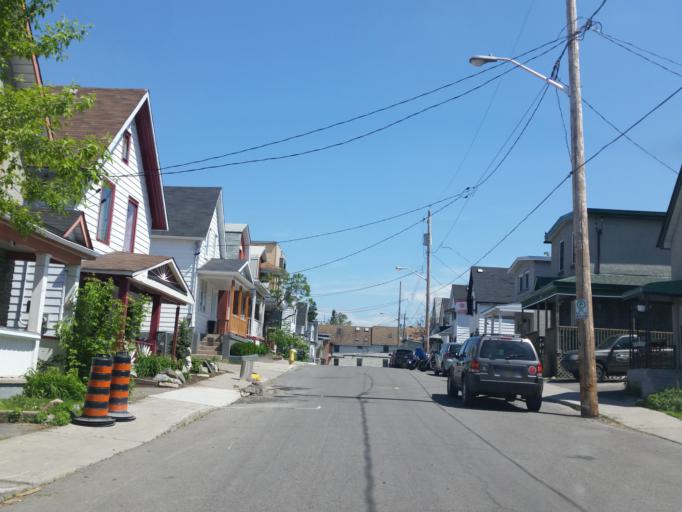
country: CA
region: Ontario
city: Ottawa
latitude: 45.4055
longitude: -75.7252
